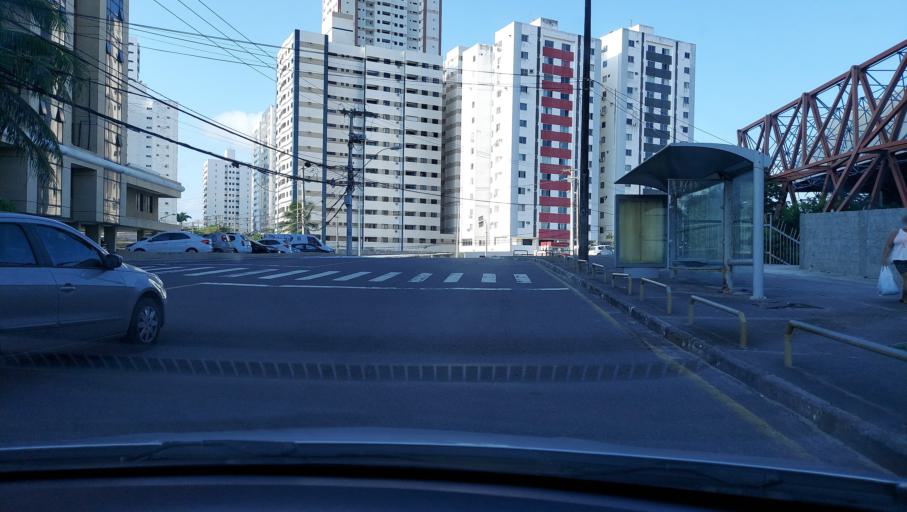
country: BR
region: Bahia
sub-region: Salvador
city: Salvador
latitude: -12.9825
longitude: -38.4413
